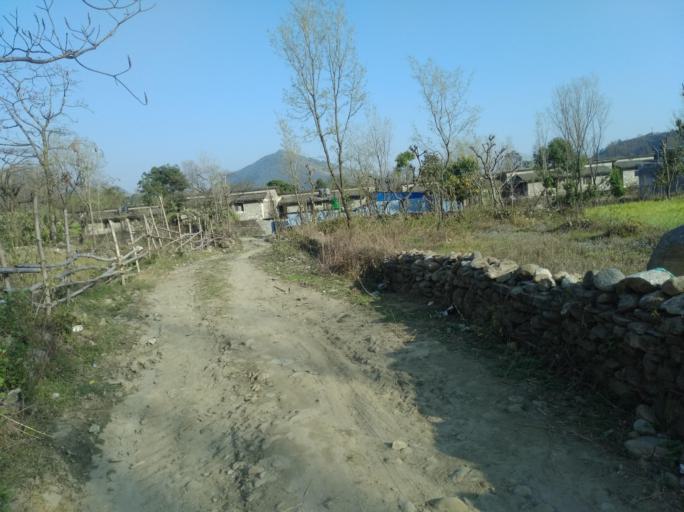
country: NP
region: Western Region
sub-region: Gandaki Zone
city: Pokhara
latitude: 28.2546
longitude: 83.9729
